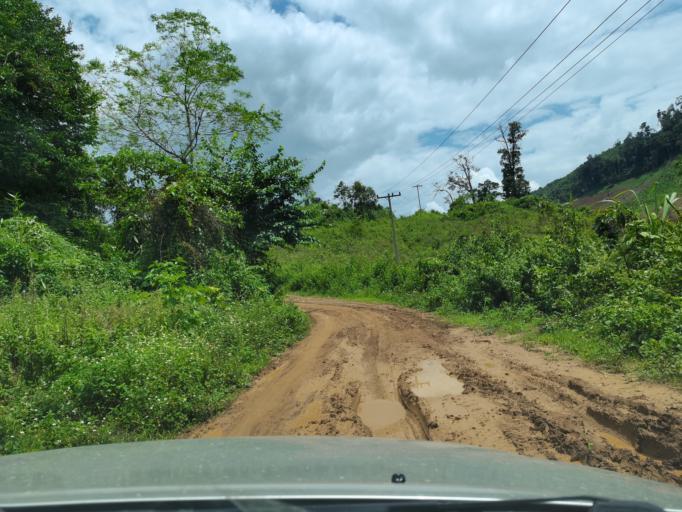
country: LA
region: Loungnamtha
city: Muang Long
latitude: 20.7300
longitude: 101.0145
